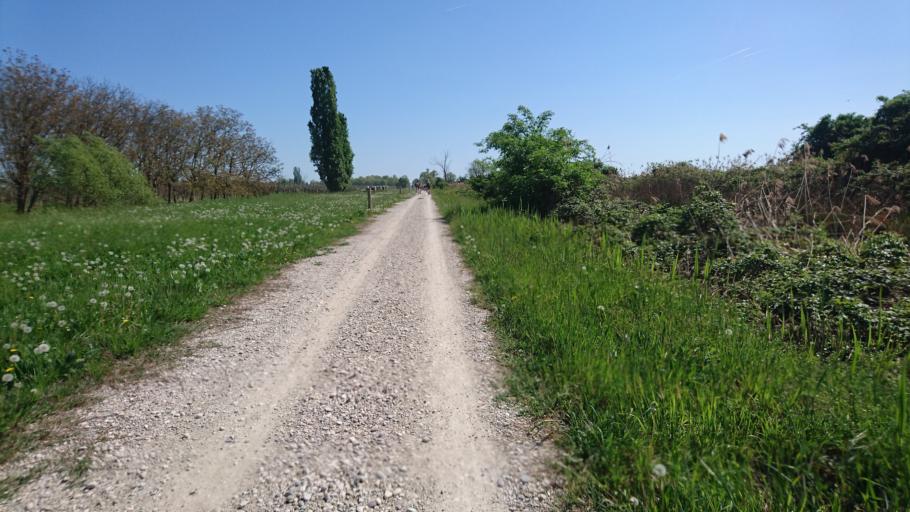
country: IT
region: Veneto
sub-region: Provincia di Venezia
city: Passarella
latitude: 45.5623
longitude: 12.5643
